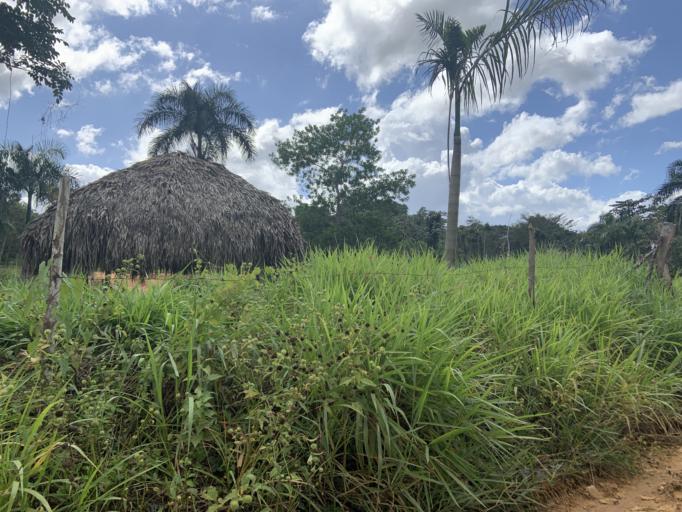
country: DO
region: Monte Plata
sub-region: Yamasa
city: Yamasa
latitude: 18.7814
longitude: -70.0278
